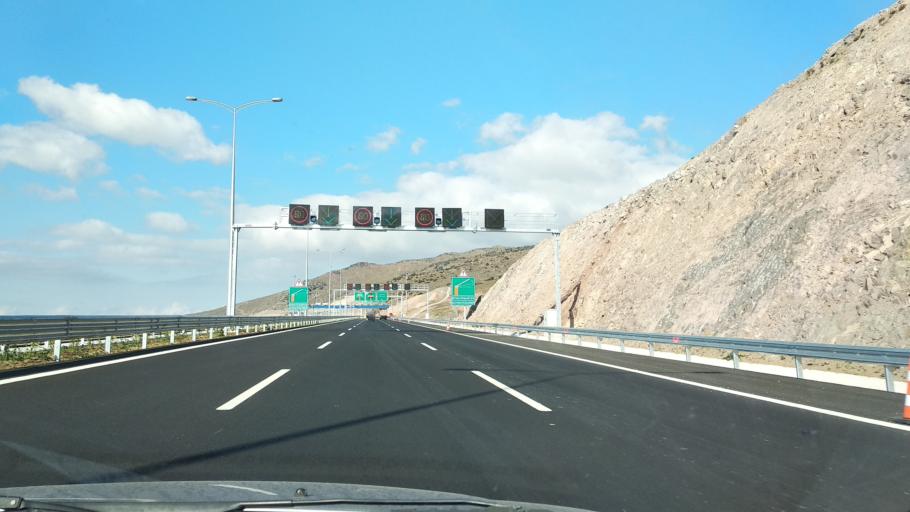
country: TR
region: Izmir
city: Menemen
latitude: 38.6698
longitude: 27.0670
